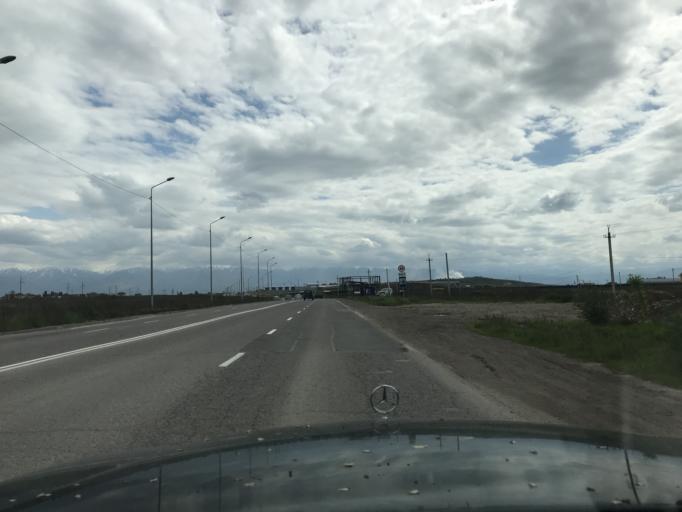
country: KZ
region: Almaty Oblysy
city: Burunday
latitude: 43.3506
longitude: 76.8341
